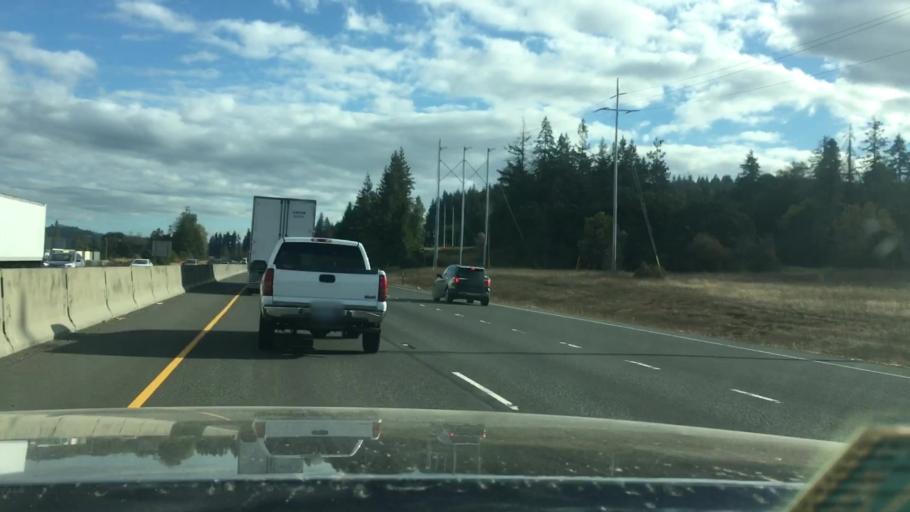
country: US
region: Oregon
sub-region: Lane County
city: Springfield
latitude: 44.0090
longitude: -123.0218
